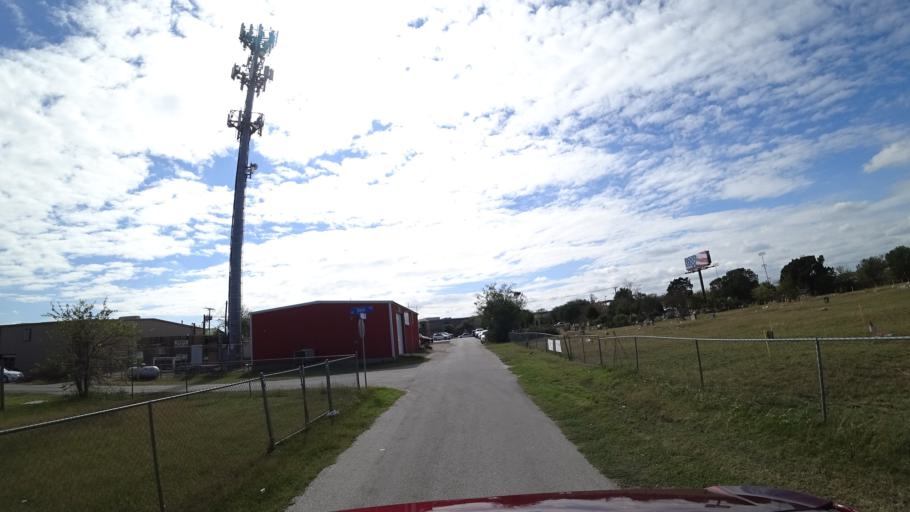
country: US
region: Texas
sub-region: Travis County
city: Pflugerville
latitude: 30.4460
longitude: -97.6311
